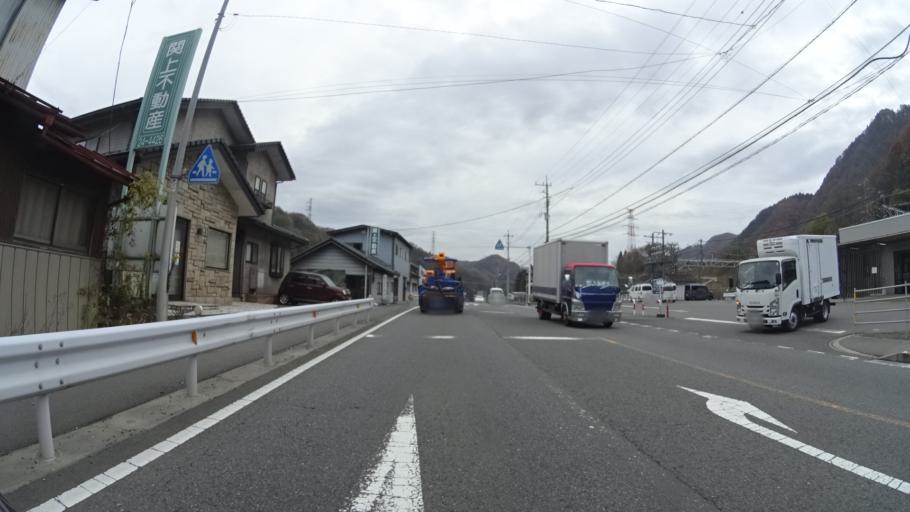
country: JP
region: Gunma
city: Numata
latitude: 36.6035
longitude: 139.0472
